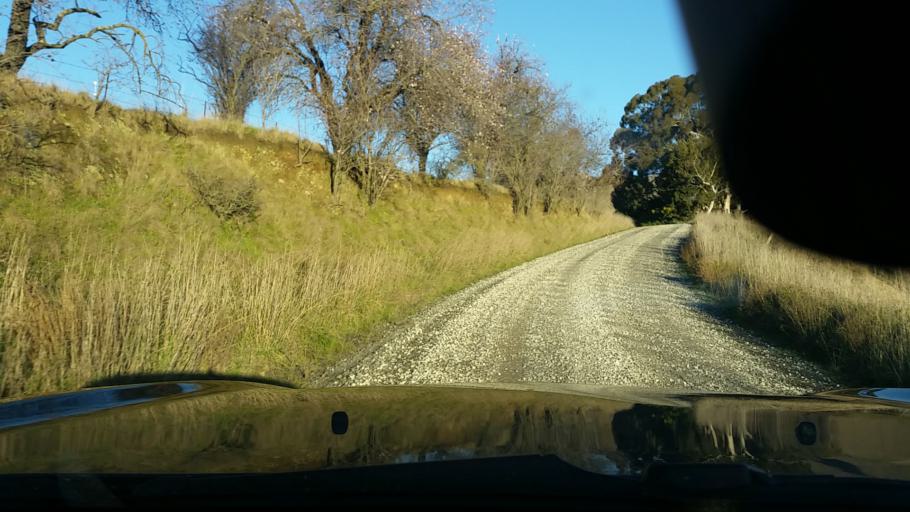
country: NZ
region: Marlborough
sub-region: Marlborough District
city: Blenheim
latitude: -41.7313
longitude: 174.0366
